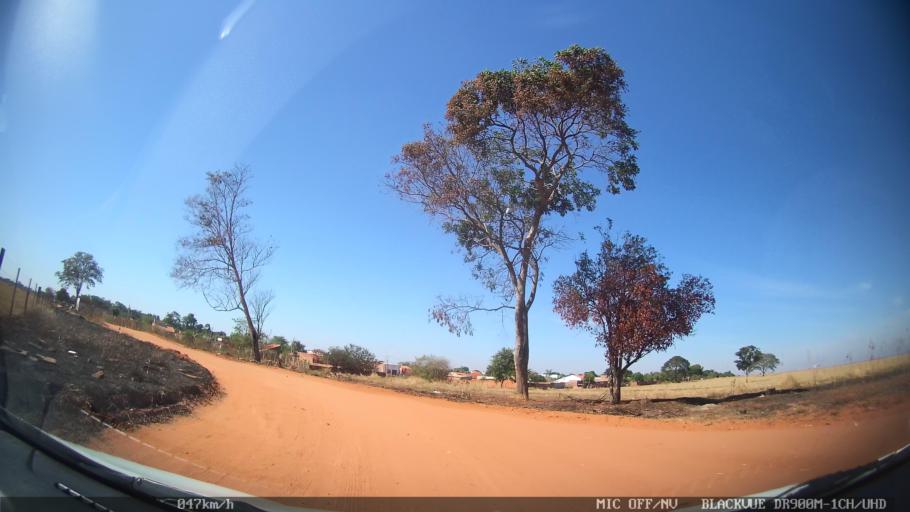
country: BR
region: Sao Paulo
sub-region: Sao Jose Do Rio Preto
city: Sao Jose do Rio Preto
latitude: -20.7445
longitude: -49.4332
